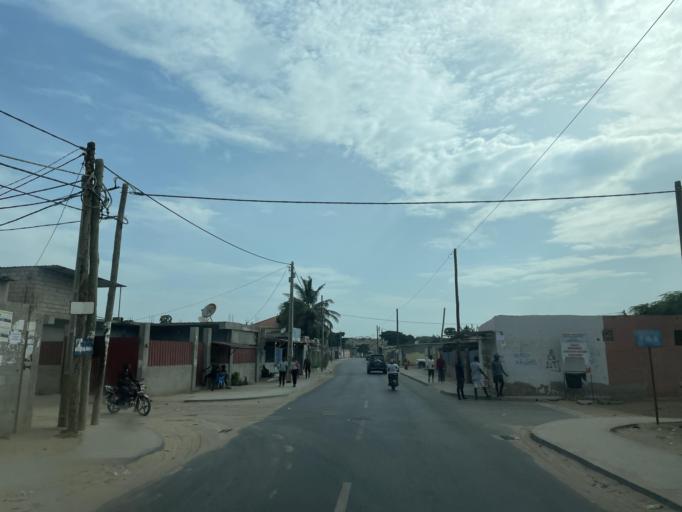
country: AO
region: Luanda
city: Luanda
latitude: -8.9324
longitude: 13.2005
